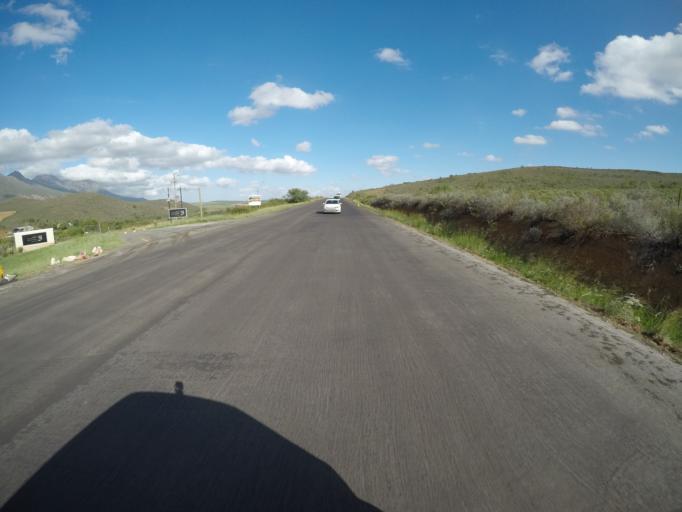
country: ZA
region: Western Cape
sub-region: Cape Winelands District Municipality
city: Ashton
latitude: -33.9276
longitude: 20.2065
